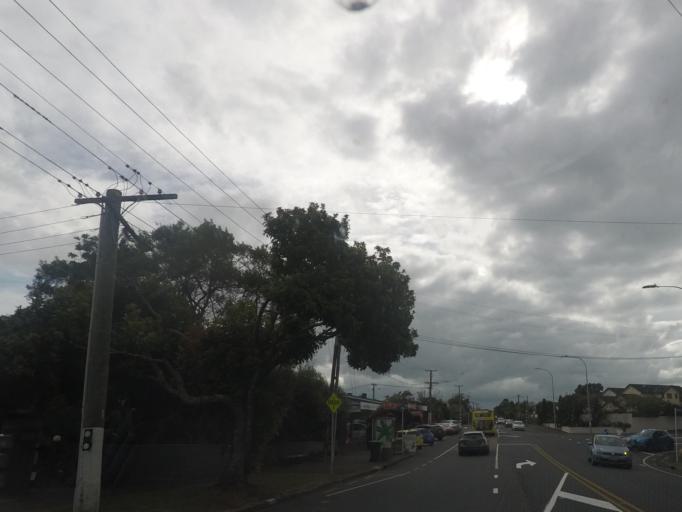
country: NZ
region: Auckland
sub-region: Auckland
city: Tamaki
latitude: -36.8665
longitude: 174.8513
